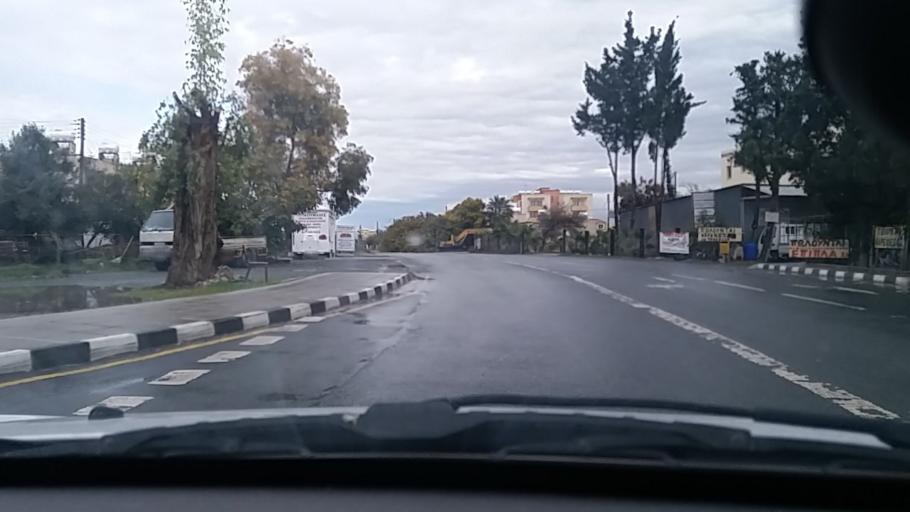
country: CY
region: Larnaka
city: Livadia
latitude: 34.9380
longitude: 33.6187
